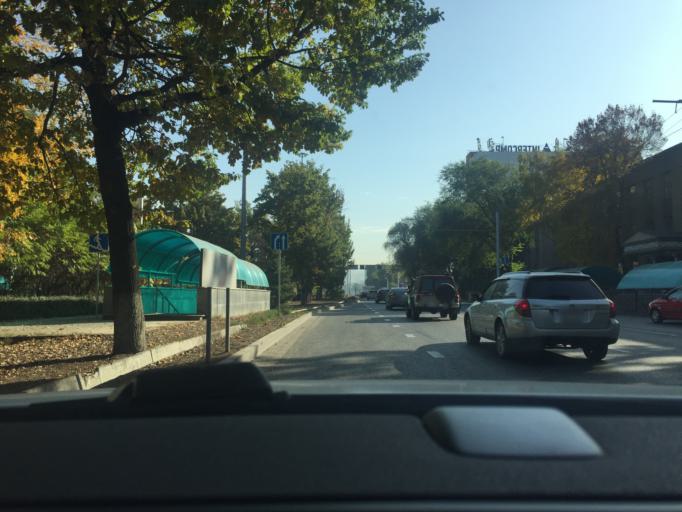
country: KZ
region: Almaty Qalasy
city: Almaty
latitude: 43.2401
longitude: 76.9123
